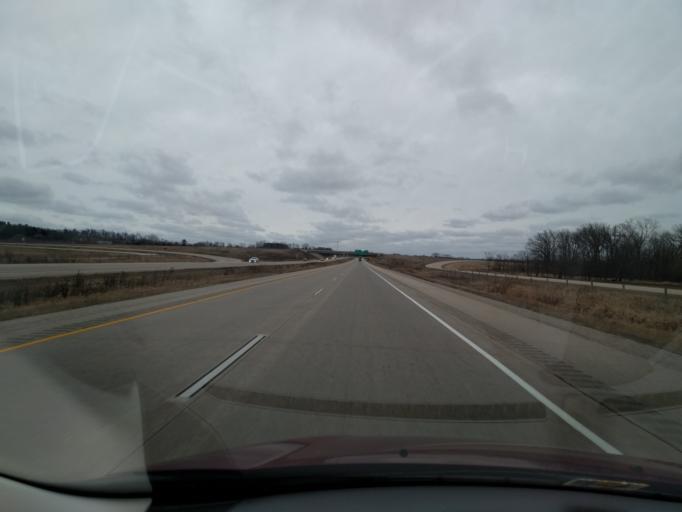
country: US
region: Wisconsin
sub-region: Winnebago County
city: Winneconne
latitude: 44.2340
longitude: -88.7455
